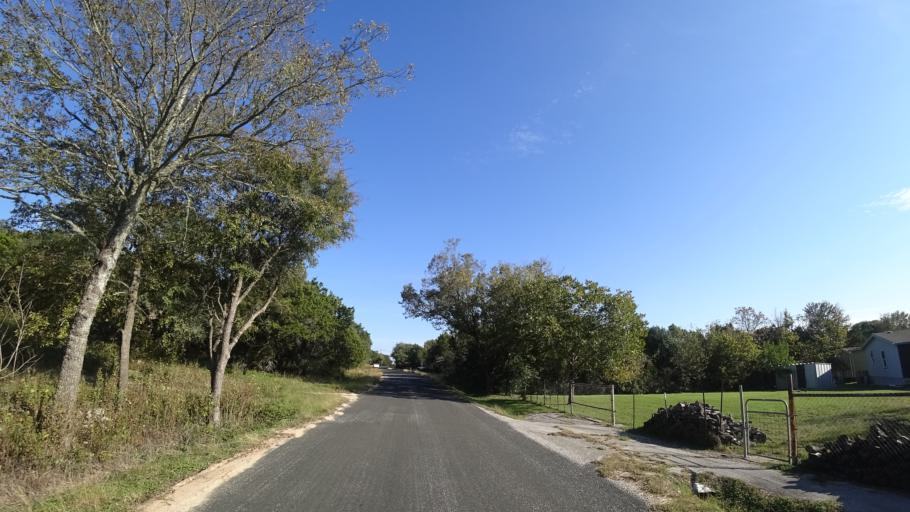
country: US
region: Texas
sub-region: Travis County
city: Barton Creek
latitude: 30.2479
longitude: -97.9138
